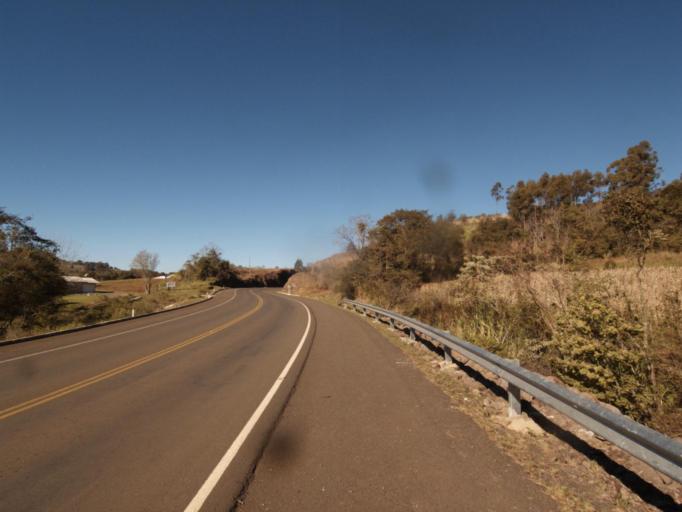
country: AR
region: Misiones
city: Bernardo de Irigoyen
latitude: -26.6969
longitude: -53.5367
